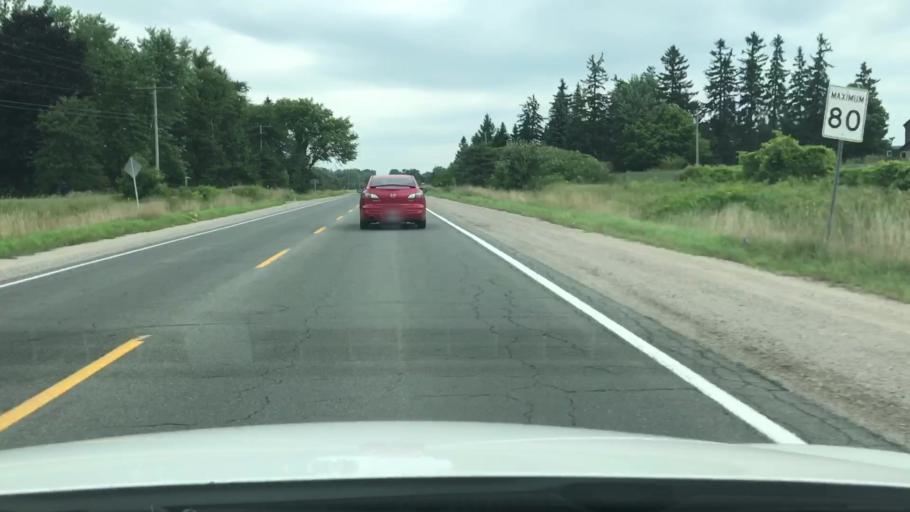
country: CA
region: Ontario
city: Innisfil
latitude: 44.3135
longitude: -79.6164
